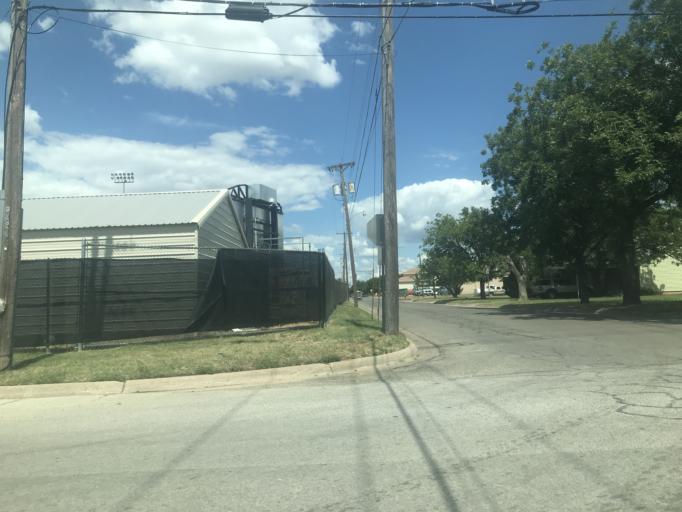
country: US
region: Texas
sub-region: Taylor County
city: Abilene
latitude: 32.4286
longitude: -99.7525
